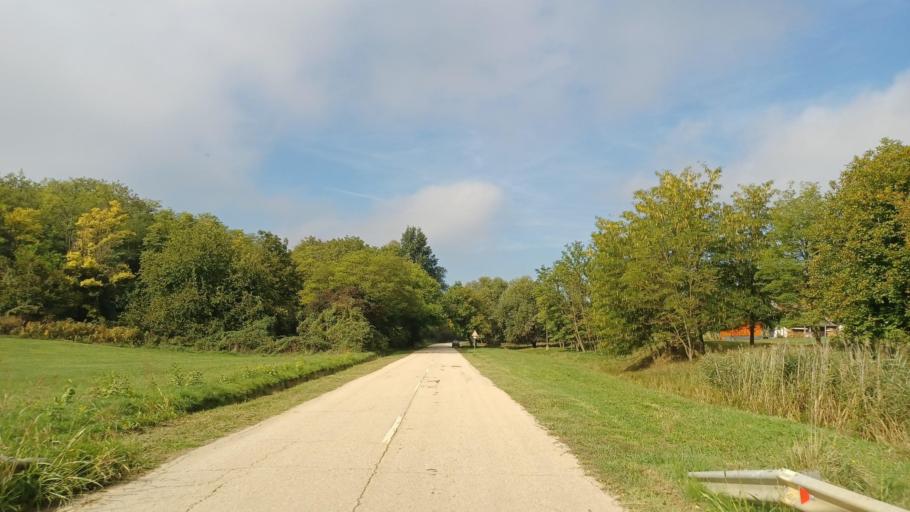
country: HU
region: Tolna
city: Pincehely
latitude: 46.6513
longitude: 18.5155
